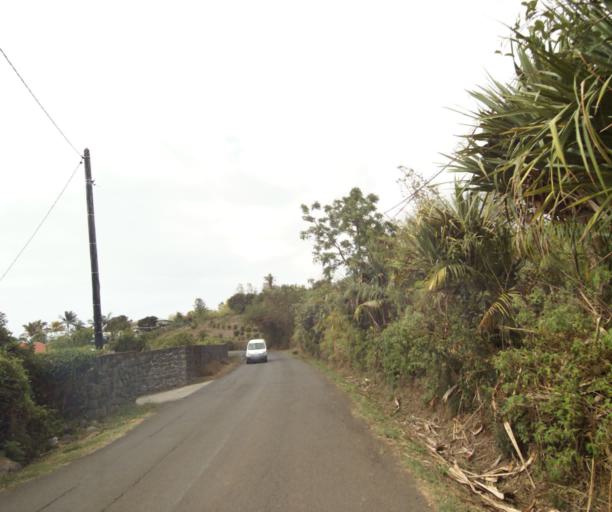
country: RE
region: Reunion
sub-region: Reunion
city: Saint-Paul
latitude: -21.0360
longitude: 55.2900
